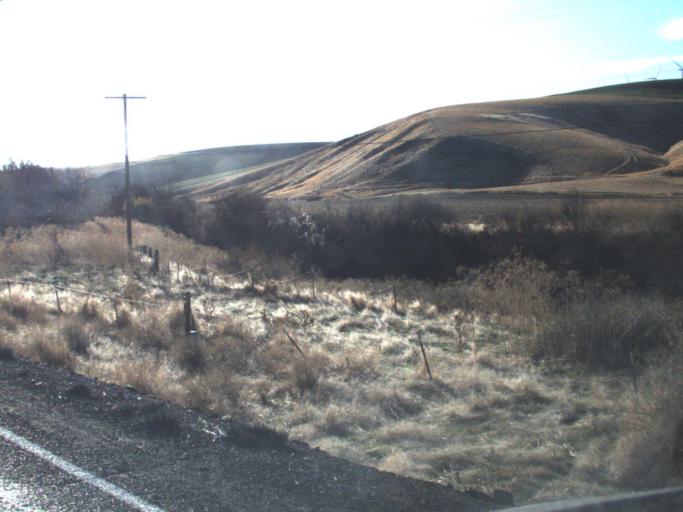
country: US
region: Washington
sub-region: Garfield County
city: Pomeroy
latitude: 46.5195
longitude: -117.7984
